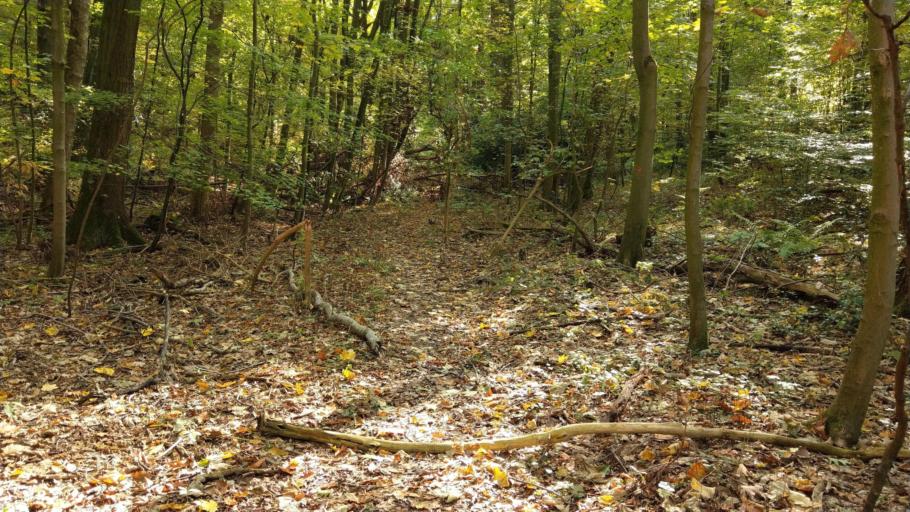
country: NL
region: Limburg
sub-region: Gemeente Vaals
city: Vaals
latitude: 50.7539
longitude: 6.0383
